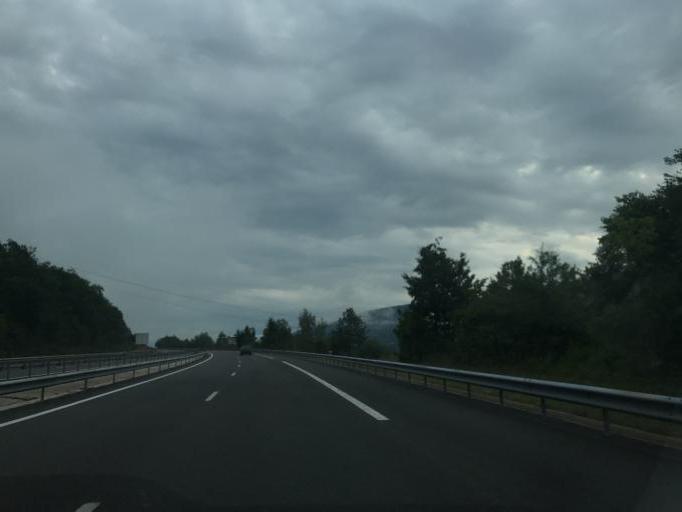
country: FR
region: Rhone-Alpes
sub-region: Departement de l'Ain
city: Montreal-la-Cluse
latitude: 46.1997
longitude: 5.5907
